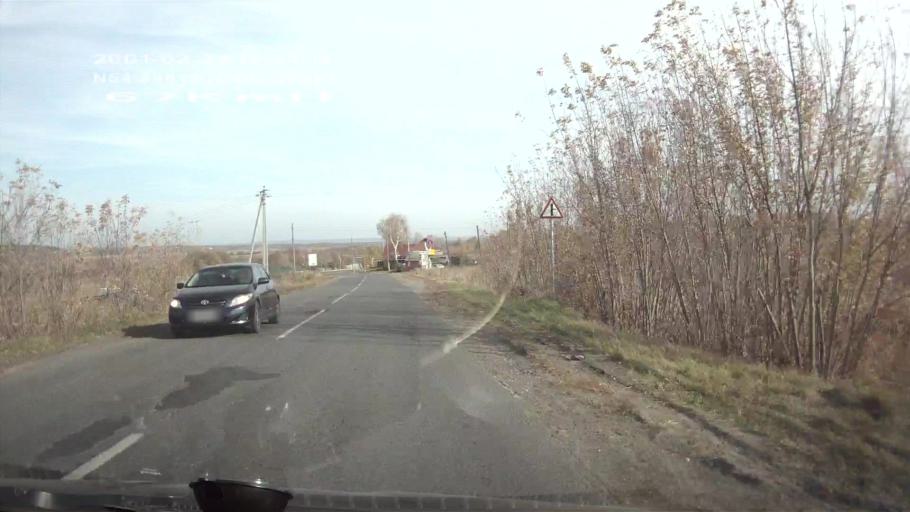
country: RU
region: Chuvashia
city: Alatyr'
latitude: 54.8462
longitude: 46.4908
